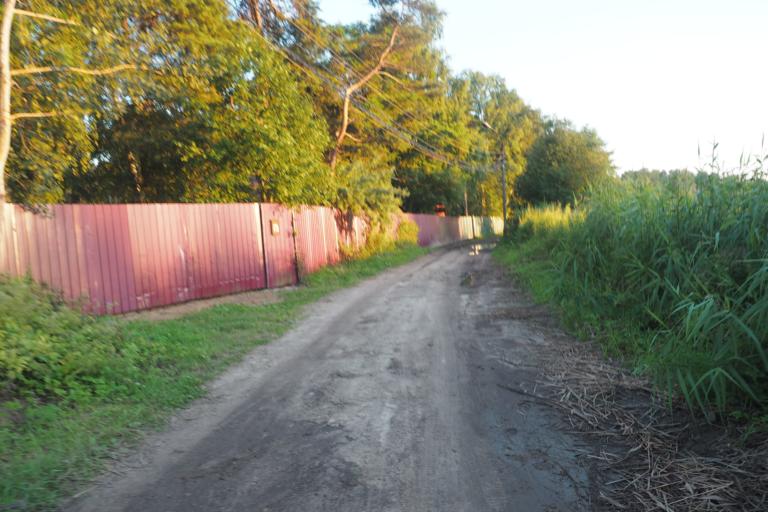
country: RU
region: Moskovskaya
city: Malyshevo
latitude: 55.5538
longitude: 38.3243
